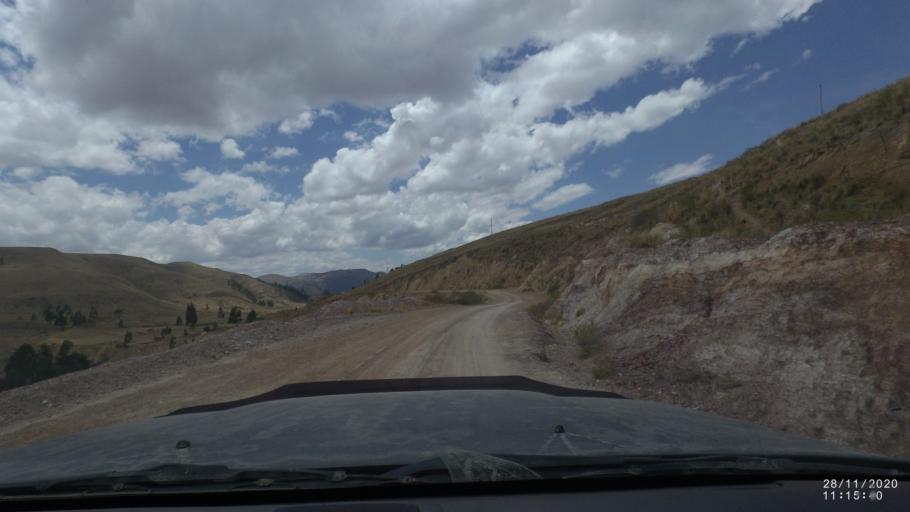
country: BO
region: Cochabamba
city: Tarata
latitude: -17.7452
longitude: -66.0876
